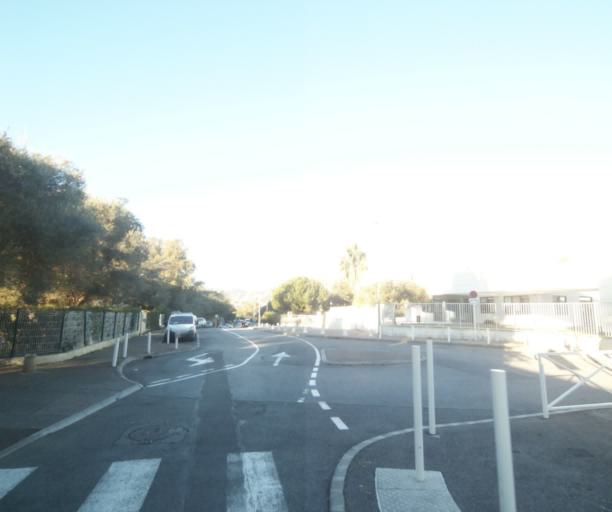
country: FR
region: Provence-Alpes-Cote d'Azur
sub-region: Departement des Alpes-Maritimes
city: Vallauris
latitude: 43.5766
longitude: 7.0915
